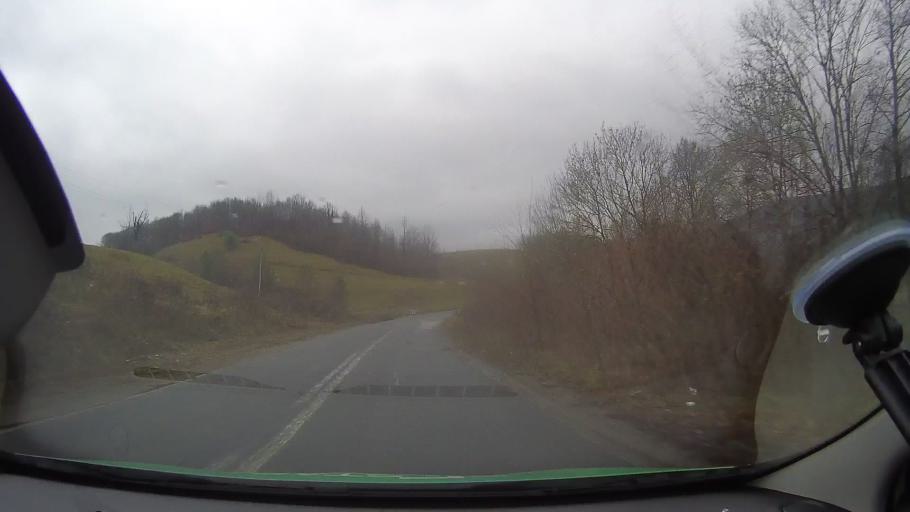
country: RO
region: Arad
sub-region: Comuna Halmagiu
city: Halmagiu
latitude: 46.2428
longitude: 22.5633
